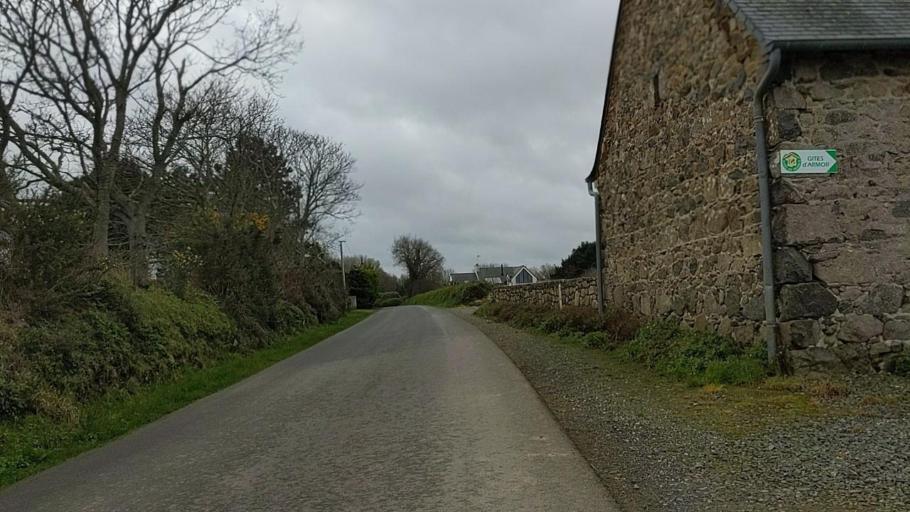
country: FR
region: Brittany
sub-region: Departement des Cotes-d'Armor
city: Pleubian
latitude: 48.8371
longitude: -3.1818
